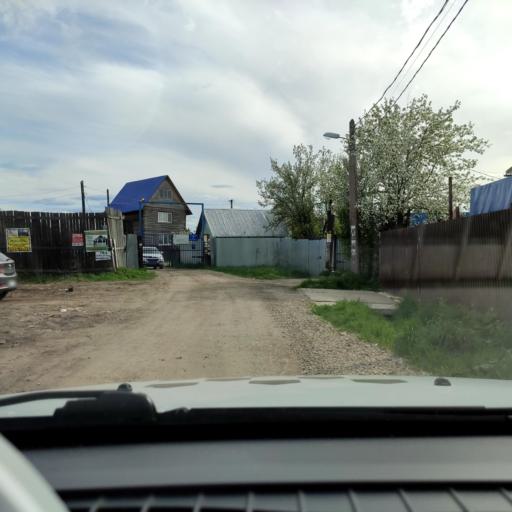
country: RU
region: Perm
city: Kondratovo
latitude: 58.0025
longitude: 56.1007
